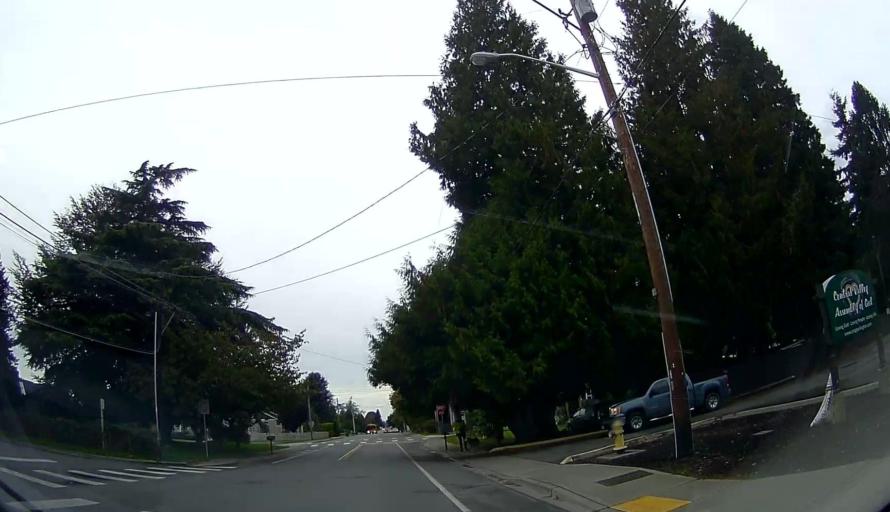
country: US
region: Washington
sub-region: Skagit County
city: Burlington
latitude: 48.4716
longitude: -122.3130
